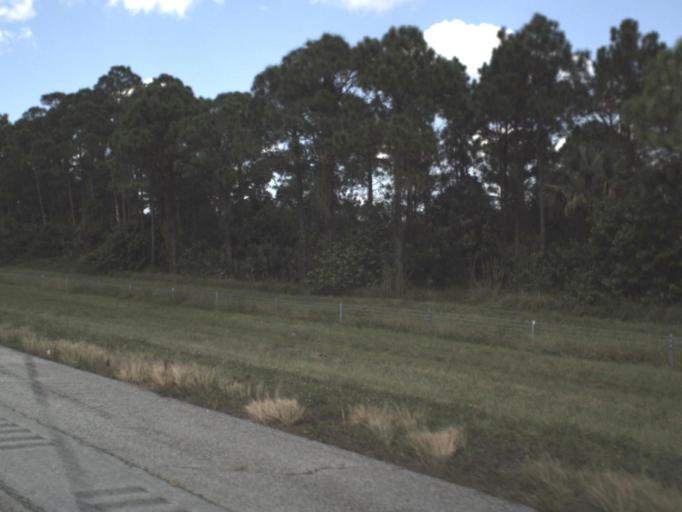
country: US
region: Florida
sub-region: Indian River County
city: West Vero Corridor
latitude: 27.5357
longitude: -80.6125
